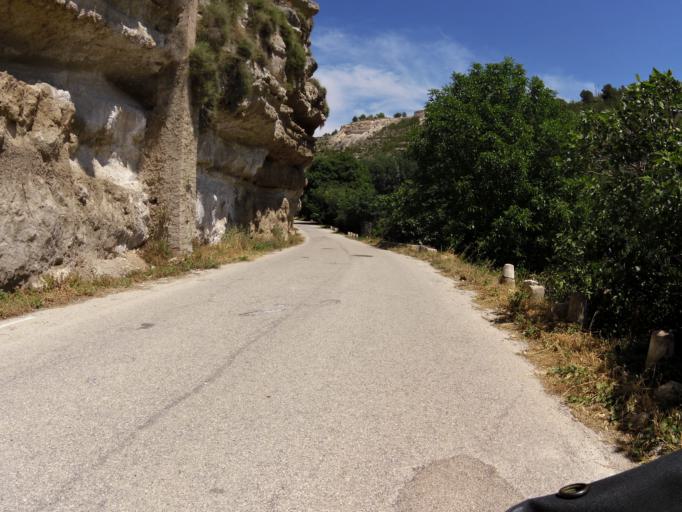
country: ES
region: Castille-La Mancha
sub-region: Provincia de Albacete
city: Jorquera
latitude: 39.1741
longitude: -1.5232
